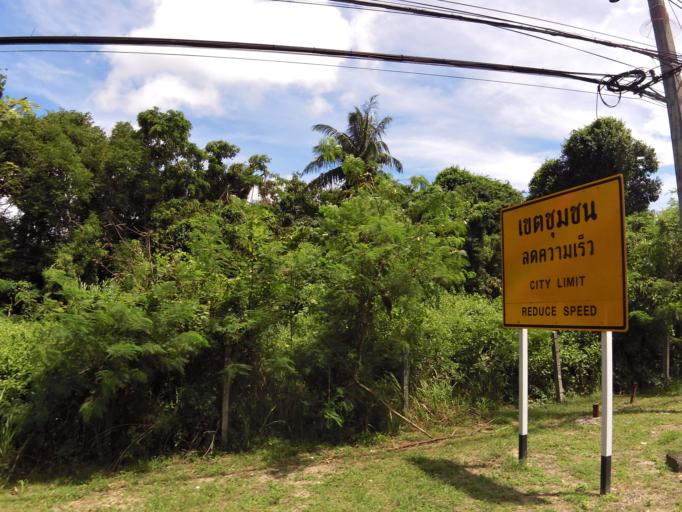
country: TH
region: Phuket
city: Ban Chalong
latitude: 7.8549
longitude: 98.3376
